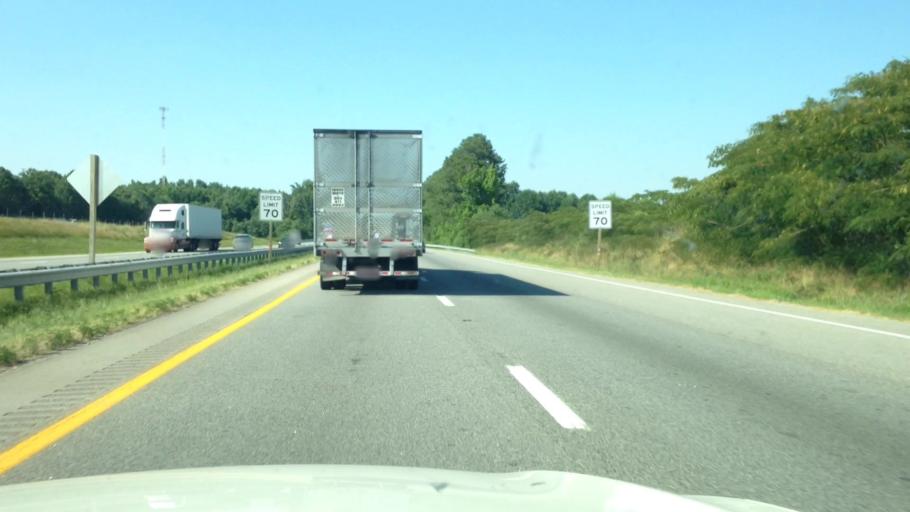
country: US
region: Virginia
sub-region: City of Emporia
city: Emporia
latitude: 36.7058
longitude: -77.5477
